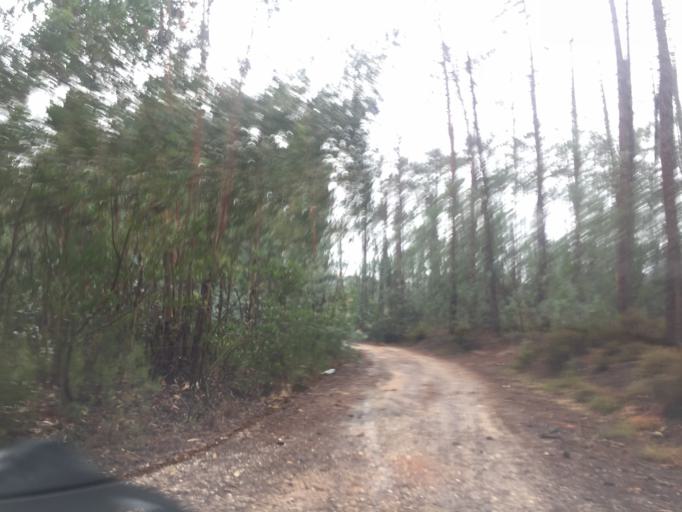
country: PT
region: Coimbra
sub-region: Figueira da Foz
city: Lavos
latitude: 40.0688
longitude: -8.7834
